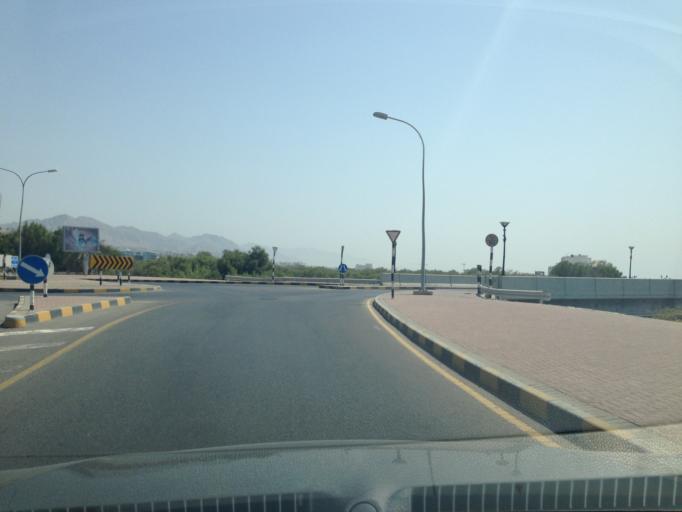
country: OM
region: Muhafazat Masqat
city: Muscat
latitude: 23.6266
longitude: 58.4833
